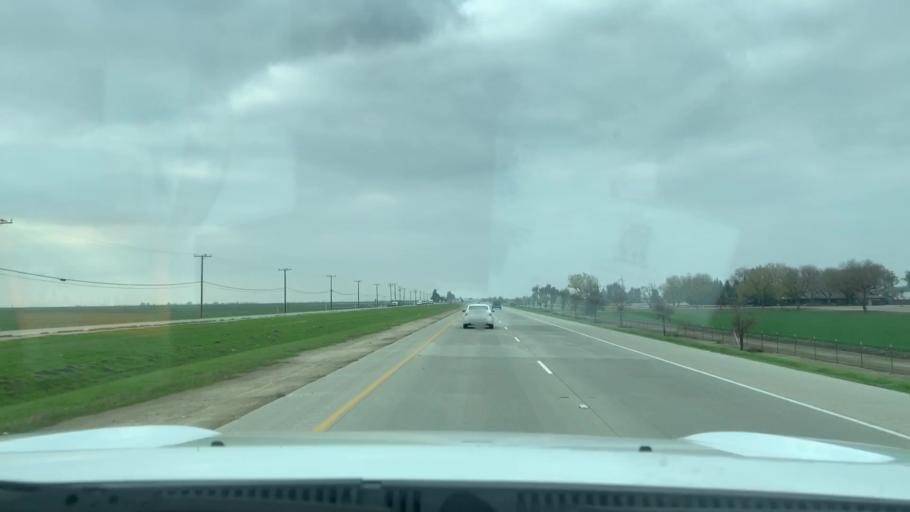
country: US
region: California
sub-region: Tulare County
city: Goshen
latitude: 36.3286
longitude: -119.5240
